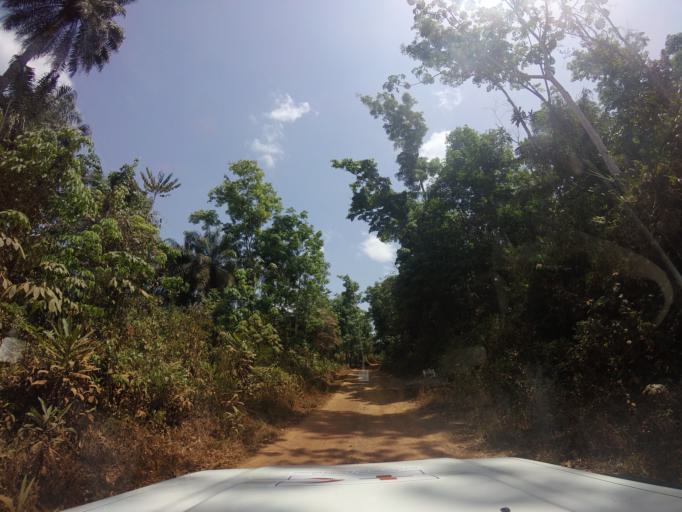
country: SL
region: Southern Province
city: Zimmi
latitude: 7.0685
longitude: -11.2731
